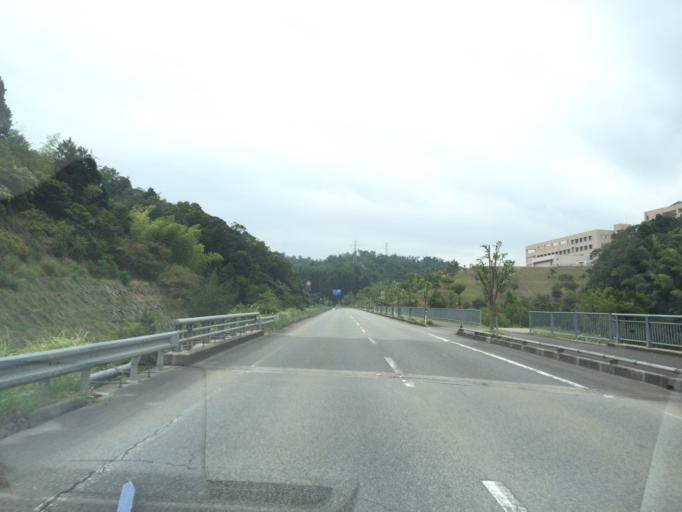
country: JP
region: Hyogo
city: Toyooka
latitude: 35.5294
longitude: 134.8087
